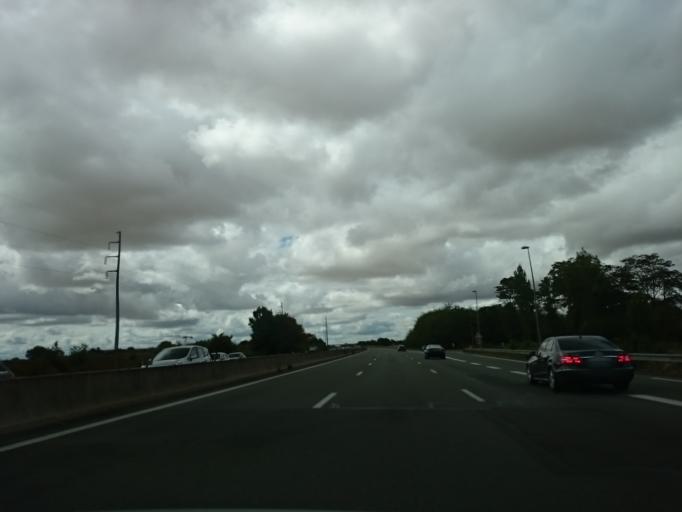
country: FR
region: Centre
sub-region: Departement d'Eure-et-Loir
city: Dammarie
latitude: 48.3633
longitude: 1.4438
